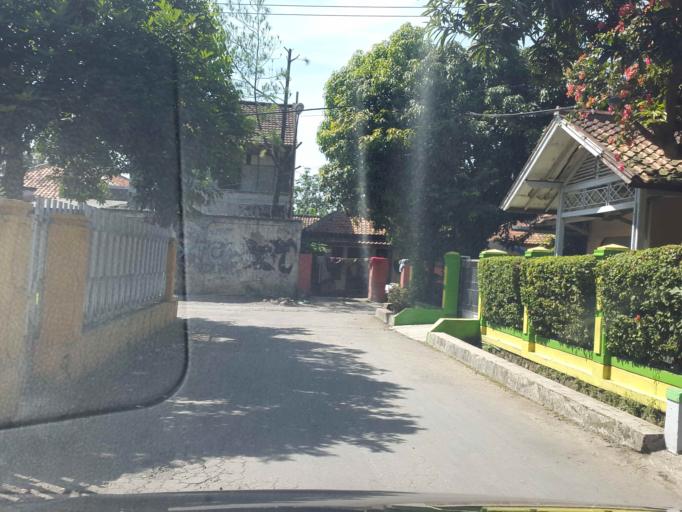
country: ID
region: West Java
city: Ciranjang-hilir
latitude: -6.7690
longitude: 107.2048
